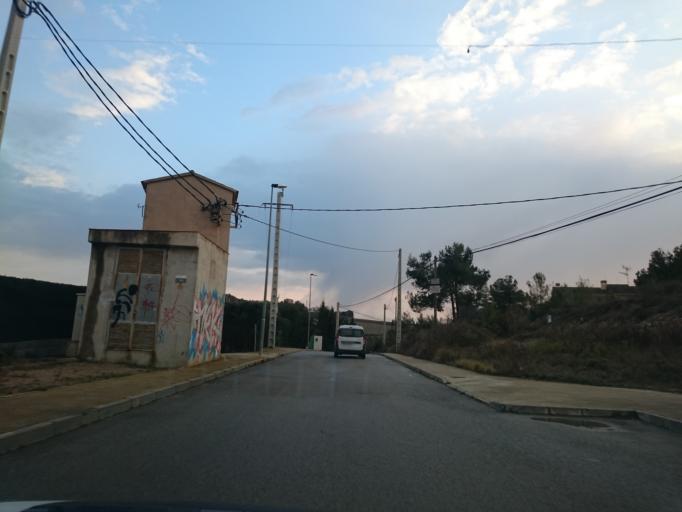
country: ES
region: Catalonia
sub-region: Provincia de Barcelona
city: Sant Marti Sarroca
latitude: 41.4176
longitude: 1.5474
